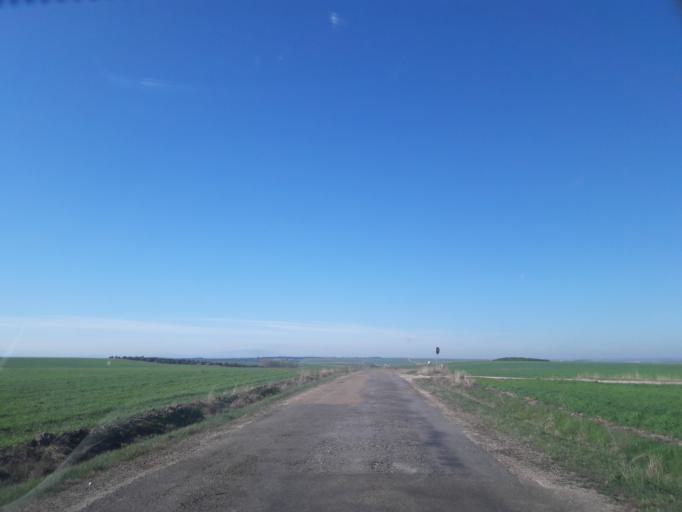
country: ES
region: Castille and Leon
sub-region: Provincia de Salamanca
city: Tordillos
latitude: 40.8698
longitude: -5.3328
